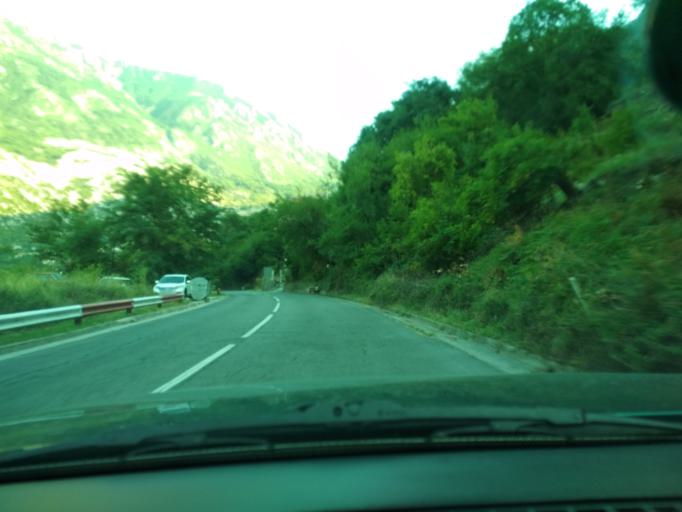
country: ME
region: Kotor
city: Kotor
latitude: 42.4199
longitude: 18.7591
